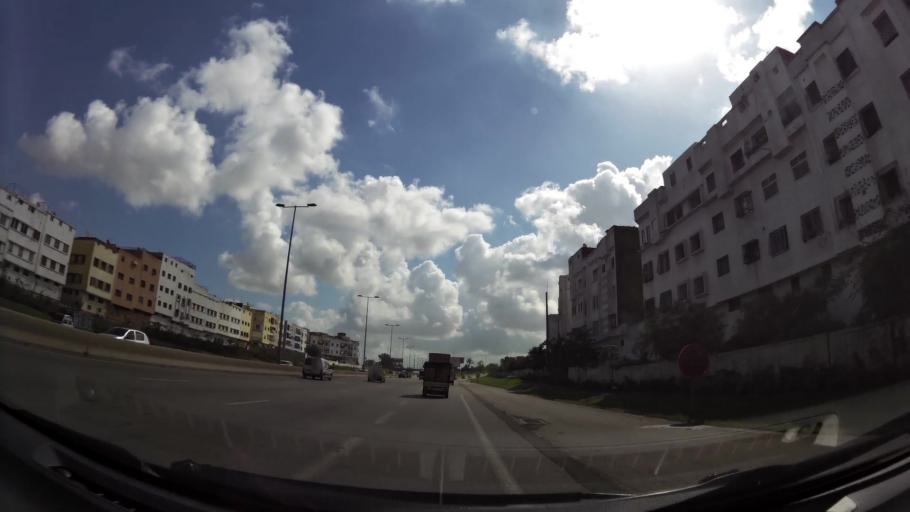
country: MA
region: Grand Casablanca
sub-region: Casablanca
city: Casablanca
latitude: 33.5585
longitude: -7.5986
